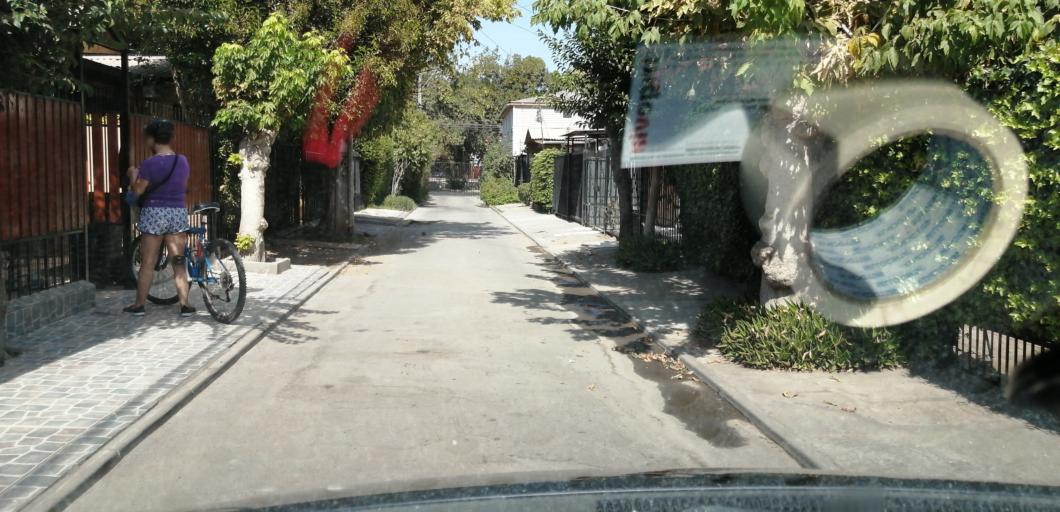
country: CL
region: Santiago Metropolitan
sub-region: Provincia de Santiago
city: Lo Prado
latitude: -33.4668
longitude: -70.7420
